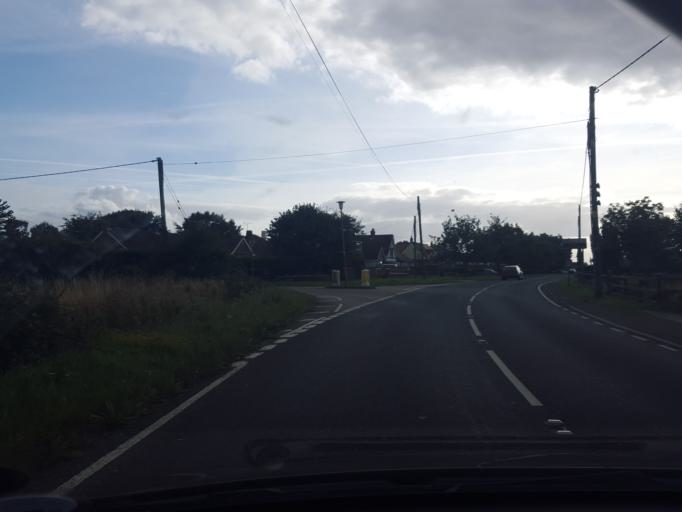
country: GB
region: England
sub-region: Essex
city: Little Clacton
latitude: 51.8416
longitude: 1.1528
